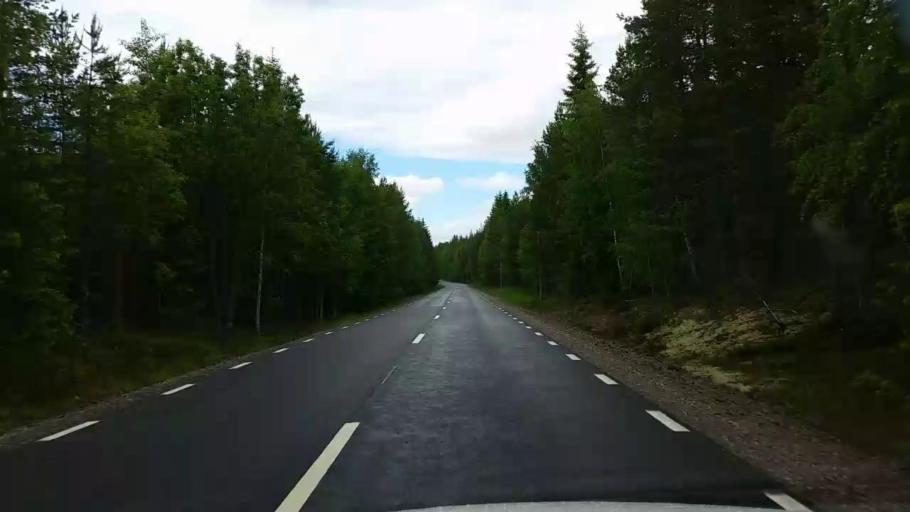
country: SE
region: Gaevleborg
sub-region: Sandvikens Kommun
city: Jarbo
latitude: 60.8562
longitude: 16.4405
